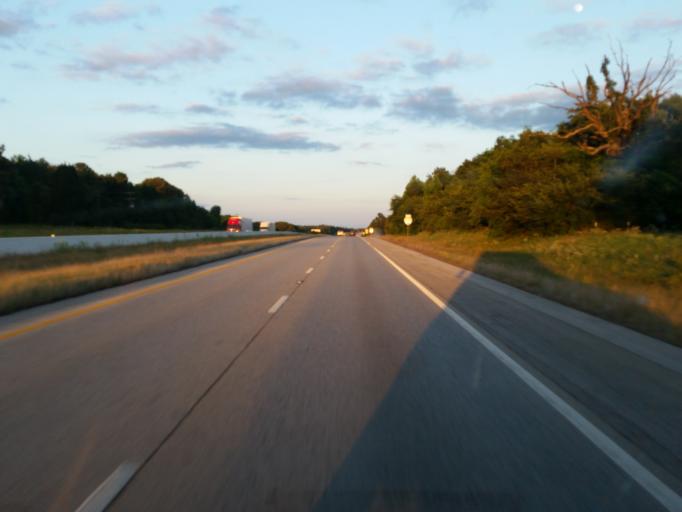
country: US
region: Texas
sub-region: Van Zandt County
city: Van
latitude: 32.4973
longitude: -95.5778
